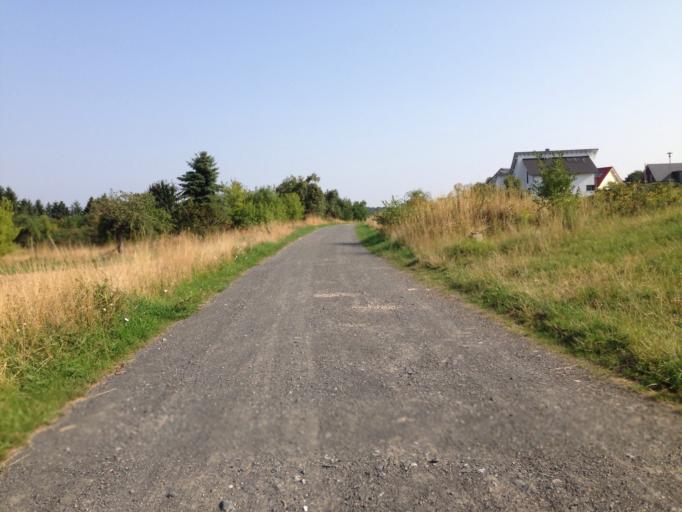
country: DE
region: Hesse
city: Lollar
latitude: 50.6145
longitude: 8.6964
